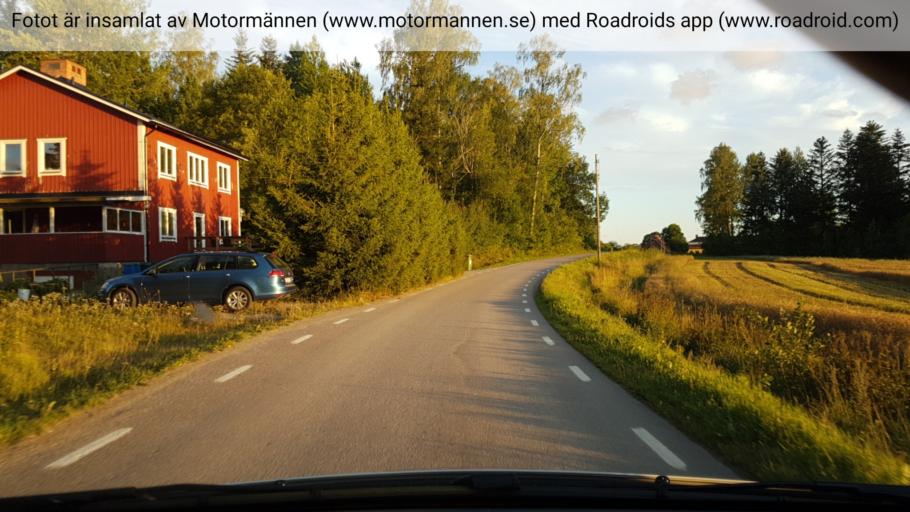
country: SE
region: Vaestmanland
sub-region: Surahammars Kommun
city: Ramnas
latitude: 59.6982
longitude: 16.0658
